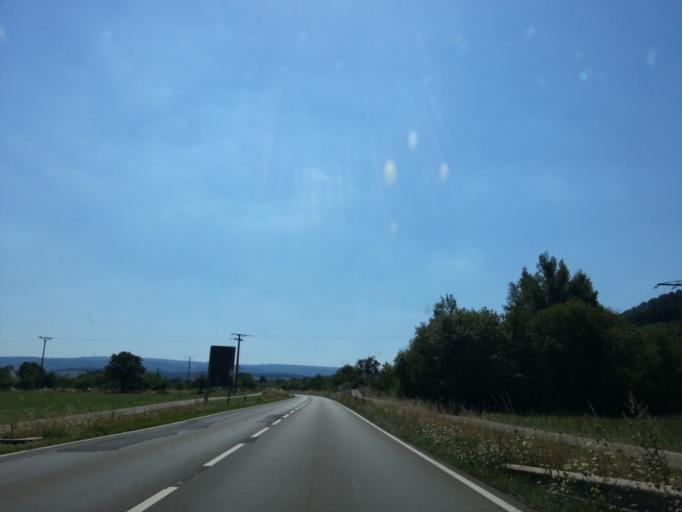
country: DE
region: Rheinland-Pfalz
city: Osann-Monzel
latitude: 49.9214
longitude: 6.9435
